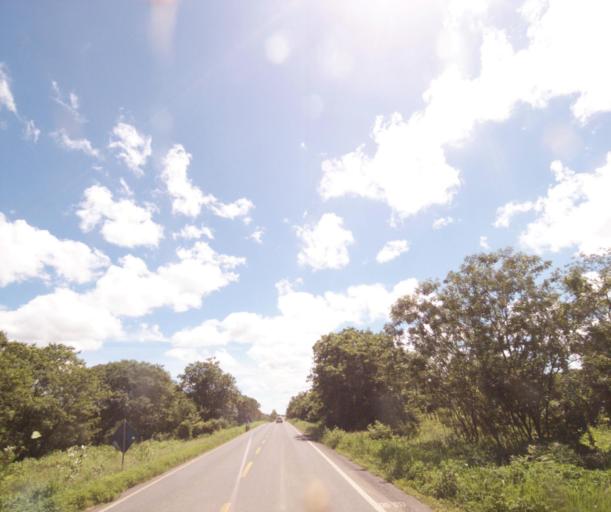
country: BR
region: Bahia
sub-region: Sao Felix Do Coribe
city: Santa Maria da Vitoria
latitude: -13.4050
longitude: -44.1543
